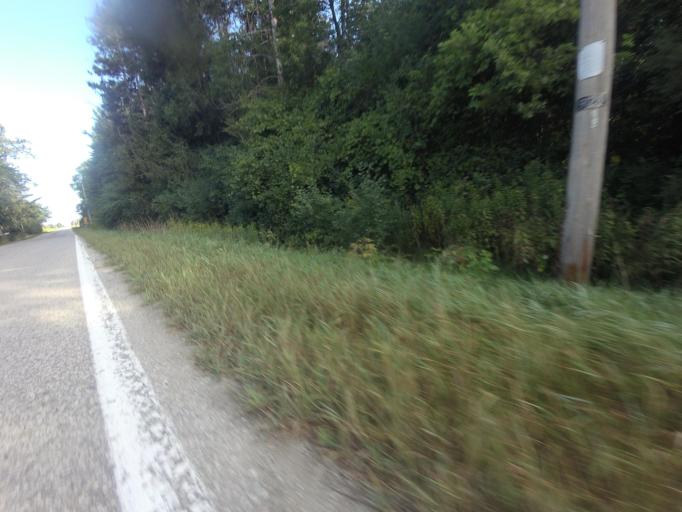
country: CA
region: Ontario
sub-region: Wellington County
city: Guelph
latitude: 43.6160
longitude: -80.3679
